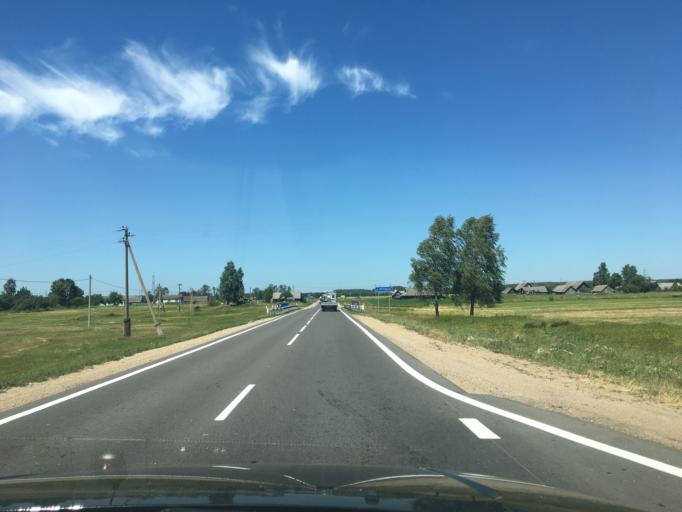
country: BY
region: Grodnenskaya
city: Hal'shany
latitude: 54.0991
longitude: 25.9160
